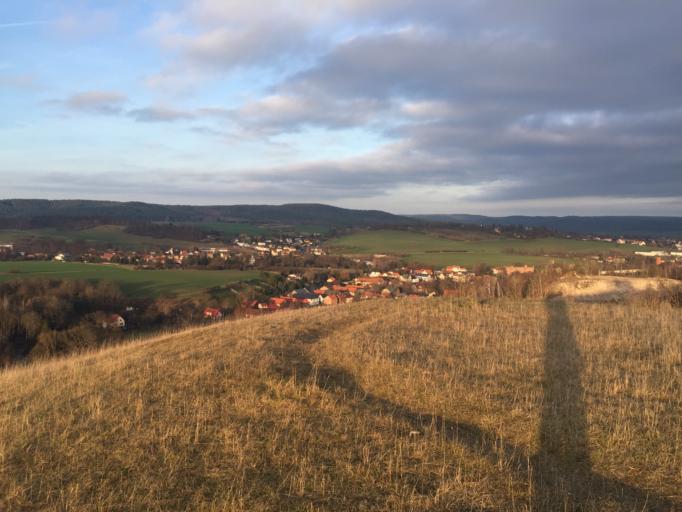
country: DE
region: Thuringia
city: Ranis
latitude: 50.6862
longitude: 11.5663
